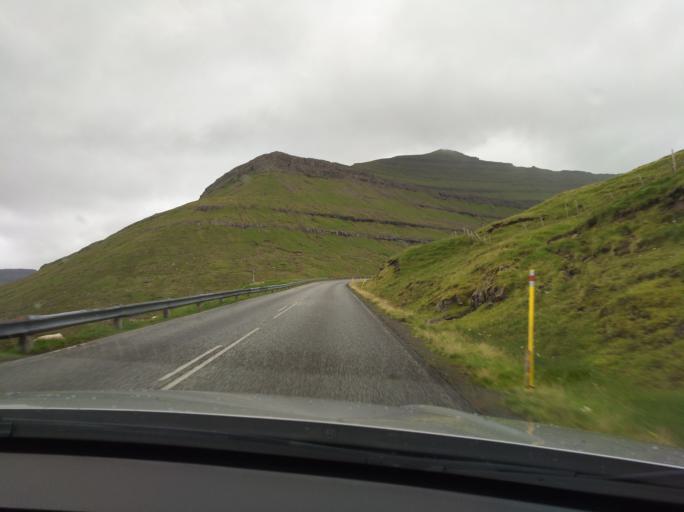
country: FO
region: Eysturoy
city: Fuglafjordur
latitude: 62.2227
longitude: -6.8770
